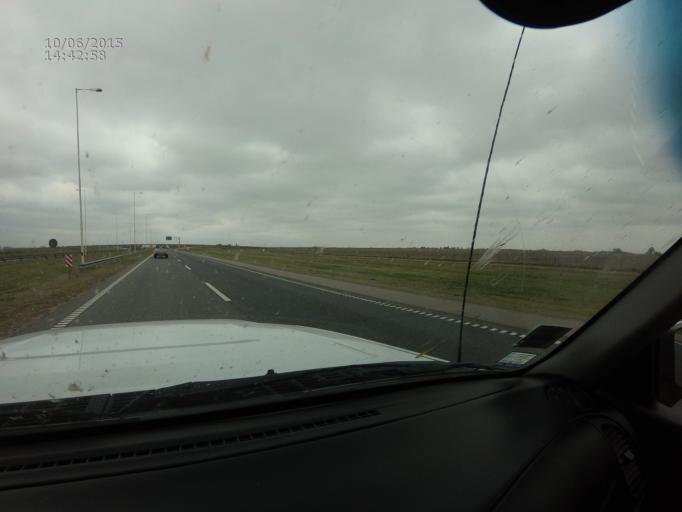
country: AR
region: Cordoba
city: Oliva
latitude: -32.0234
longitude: -63.5317
